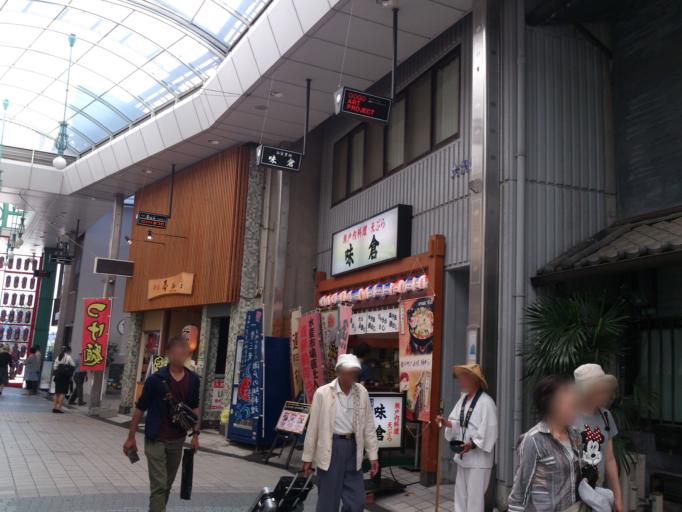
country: JP
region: Ehime
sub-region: Shikoku-chuo Shi
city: Matsuyama
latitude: 33.8513
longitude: 132.7851
